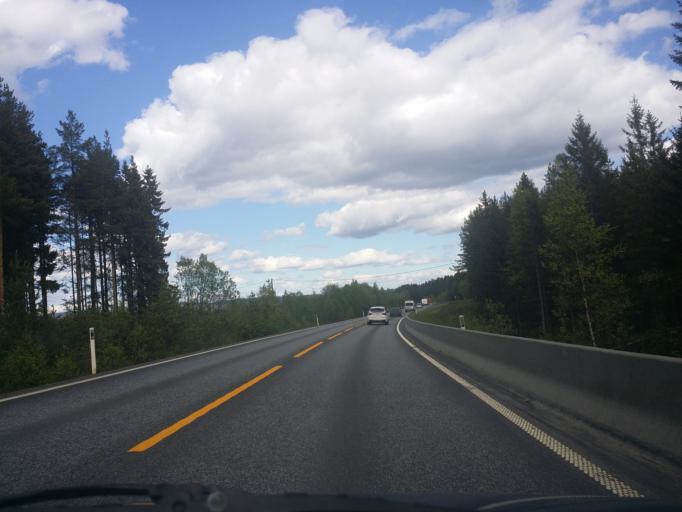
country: NO
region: Oppland
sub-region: Lunner
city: Roa
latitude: 60.2778
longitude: 10.5152
